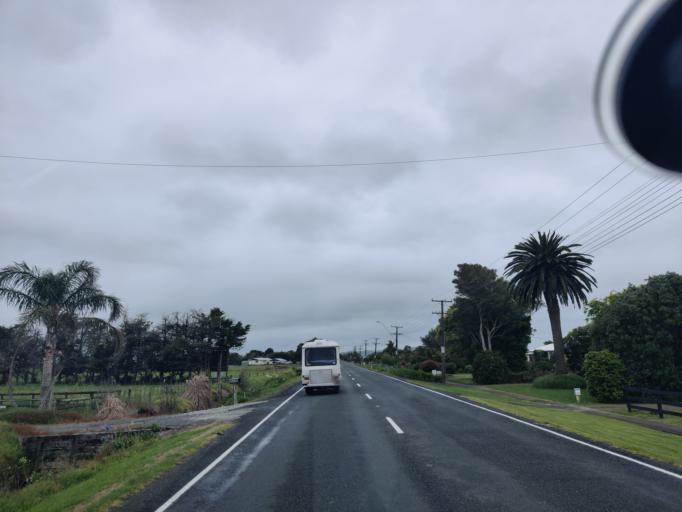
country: NZ
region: Northland
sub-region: Kaipara District
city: Dargaville
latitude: -36.1326
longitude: 174.0297
